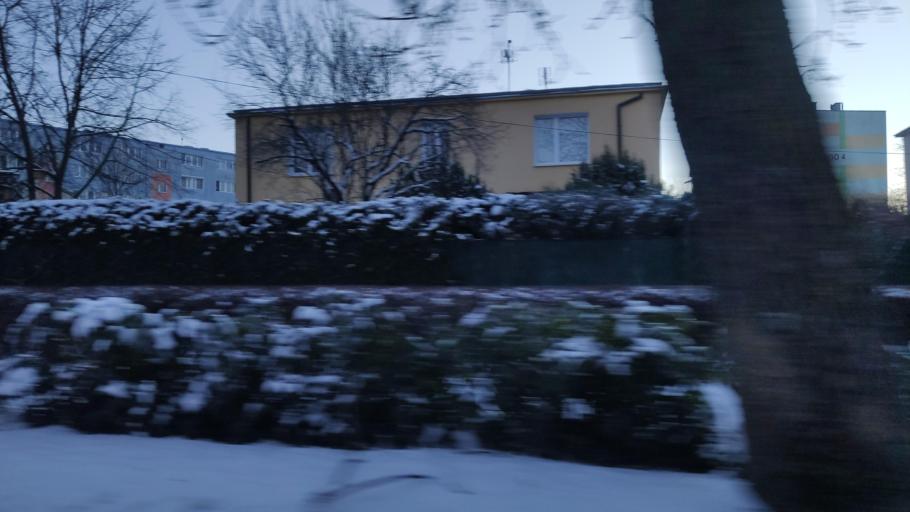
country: PL
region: Kujawsko-Pomorskie
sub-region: Powiat zninski
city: Barcin
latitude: 52.8570
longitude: 17.9441
